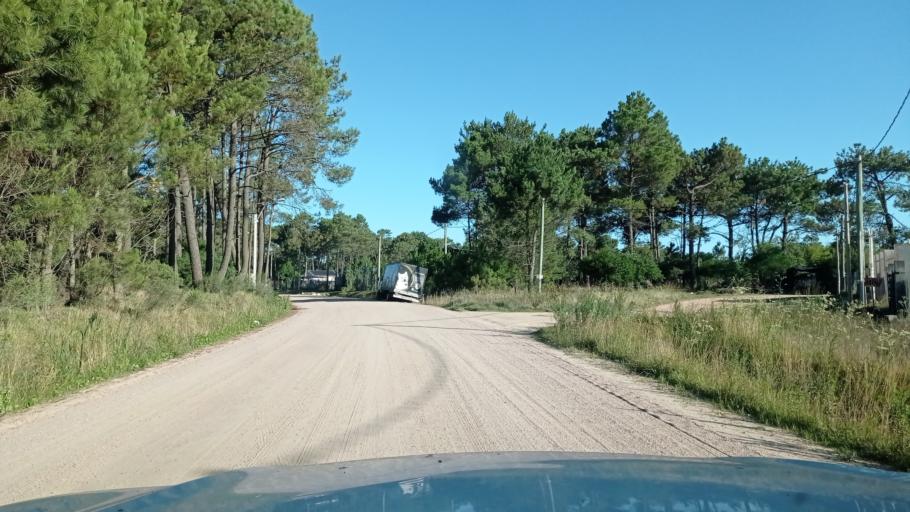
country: UY
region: Canelones
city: Pando
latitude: -34.7931
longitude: -55.9183
